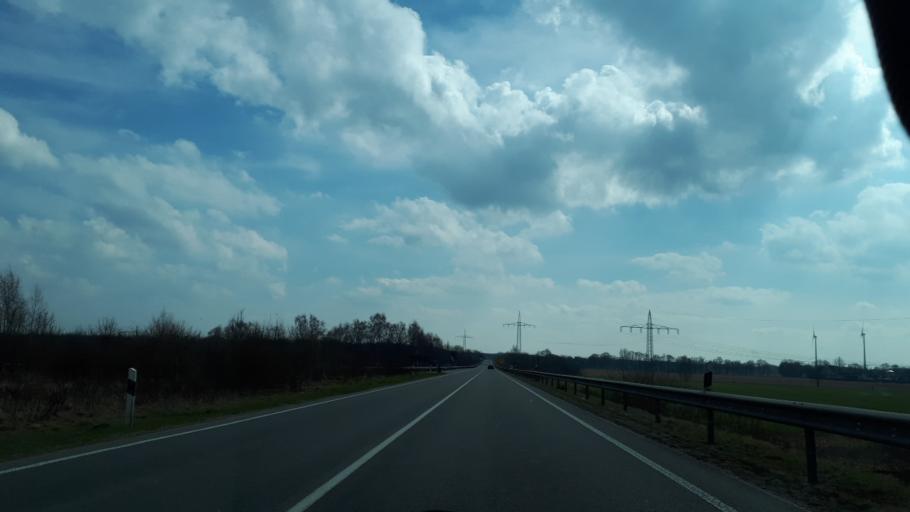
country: DE
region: Lower Saxony
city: Vechta
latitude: 52.7279
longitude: 8.2524
